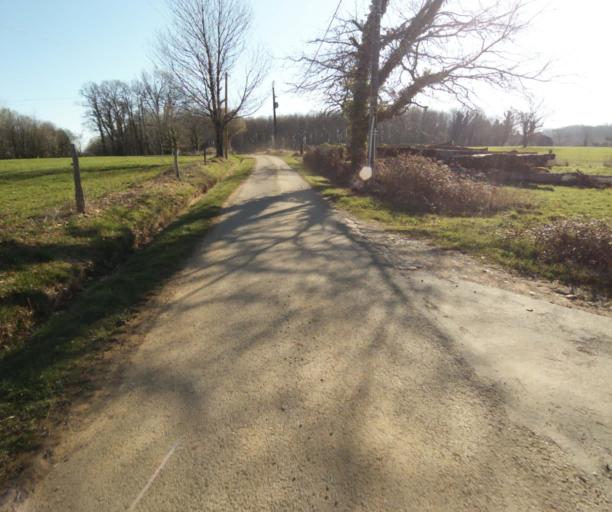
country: FR
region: Limousin
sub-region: Departement de la Correze
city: Saint-Clement
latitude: 45.3731
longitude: 1.6431
